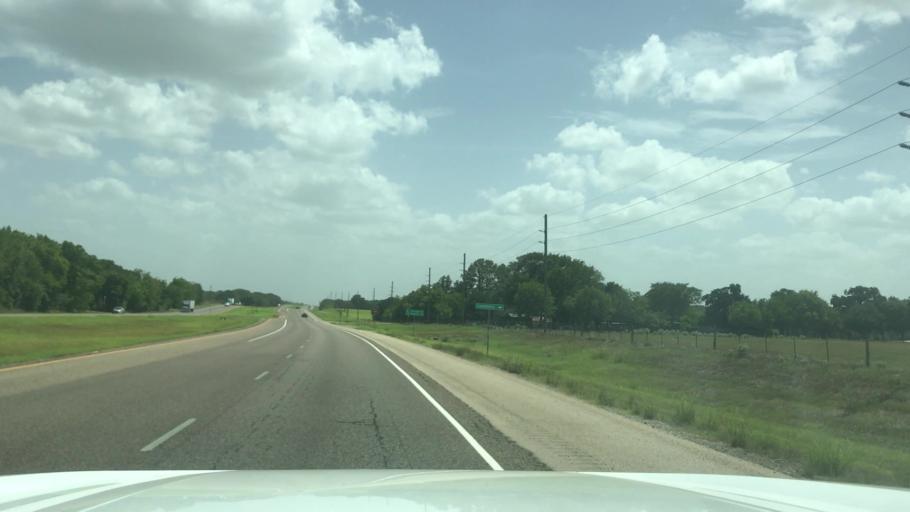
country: US
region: Texas
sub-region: Robertson County
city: Calvert
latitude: 31.0971
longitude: -96.7153
